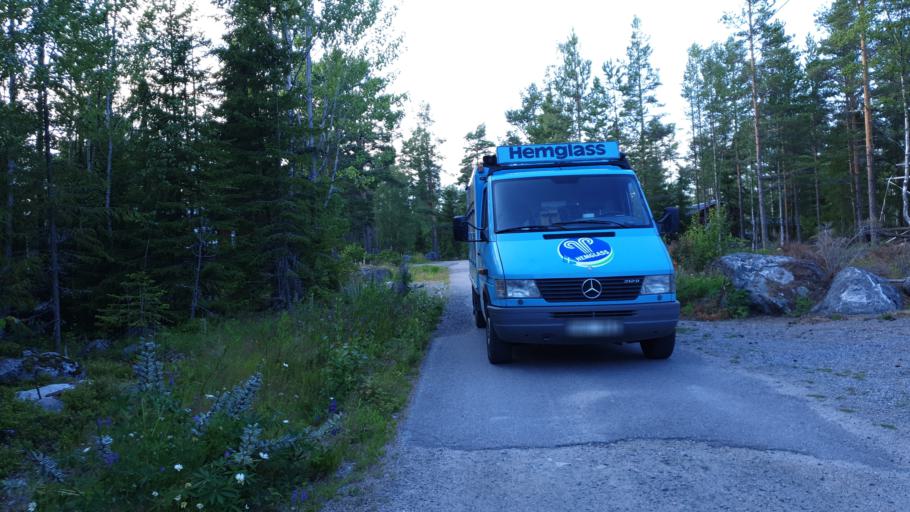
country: SE
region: Gaevleborg
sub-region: Soderhamns Kommun
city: Marielund
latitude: 61.4220
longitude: 17.1547
